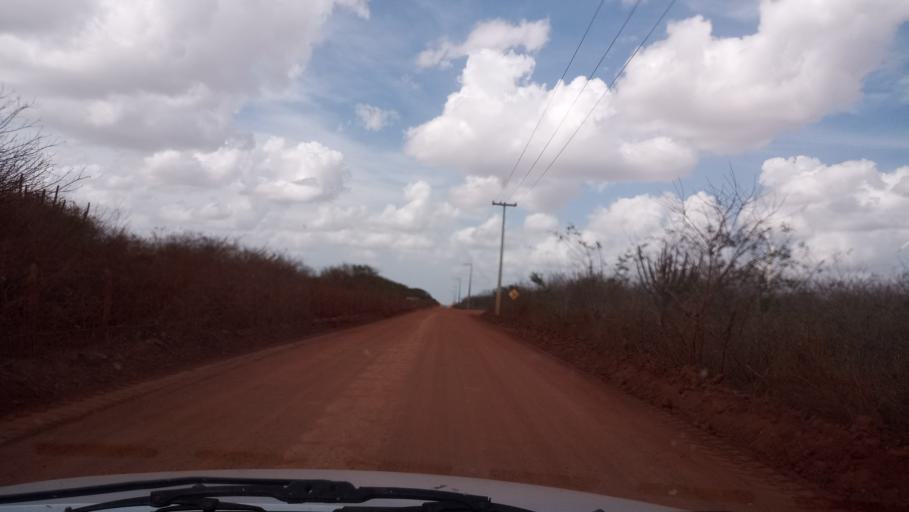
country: BR
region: Rio Grande do Norte
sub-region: Joao Camara
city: Joao Camara
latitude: -5.3588
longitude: -35.8338
